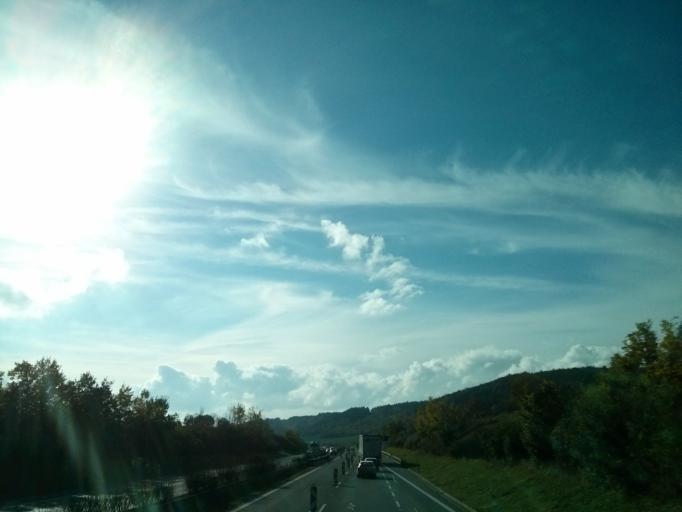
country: CZ
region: Central Bohemia
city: Zebrak
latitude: 49.8907
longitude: 13.9322
